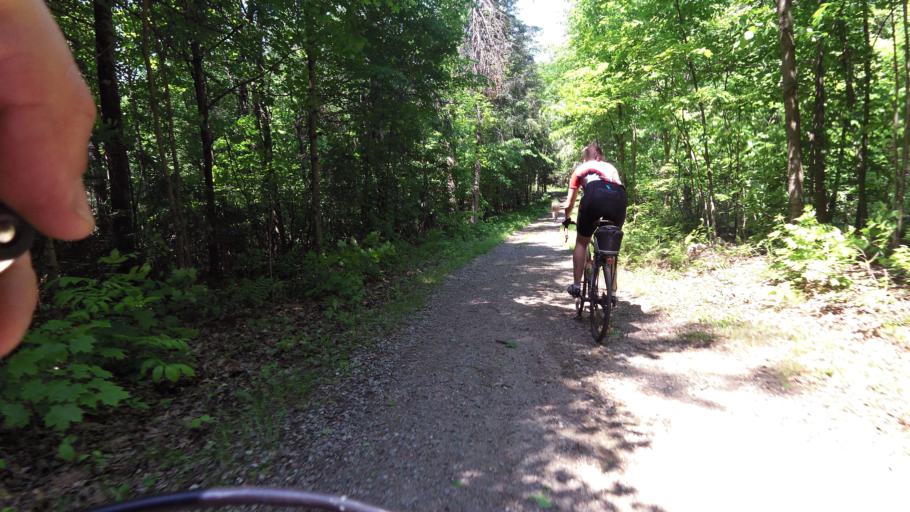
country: CA
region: Quebec
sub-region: Outaouais
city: Wakefield
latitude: 45.5682
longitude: -75.9153
